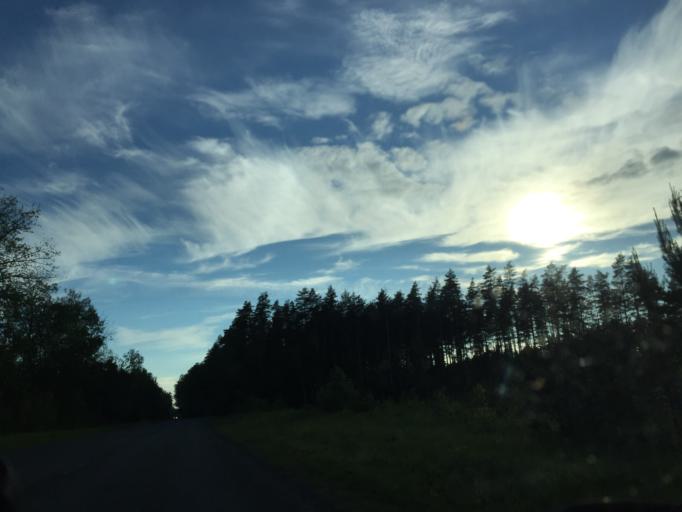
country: LV
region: Beverina
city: Murmuiza
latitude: 57.5342
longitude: 25.4796
